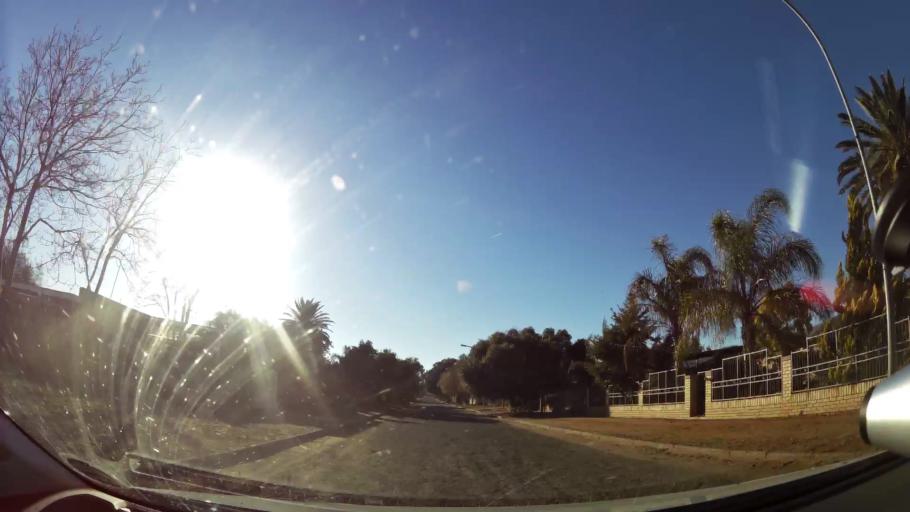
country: ZA
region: Northern Cape
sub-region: Frances Baard District Municipality
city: Kimberley
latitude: -28.7426
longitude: 24.7345
